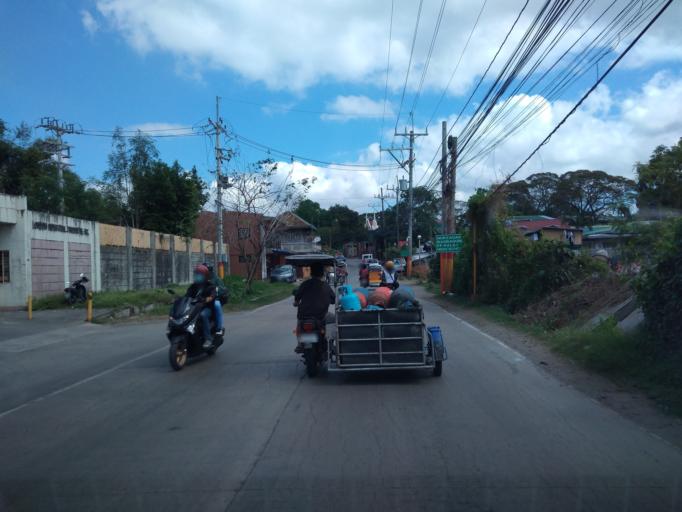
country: PH
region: Central Luzon
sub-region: Province of Bulacan
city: Guyong
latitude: 14.8338
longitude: 120.9752
